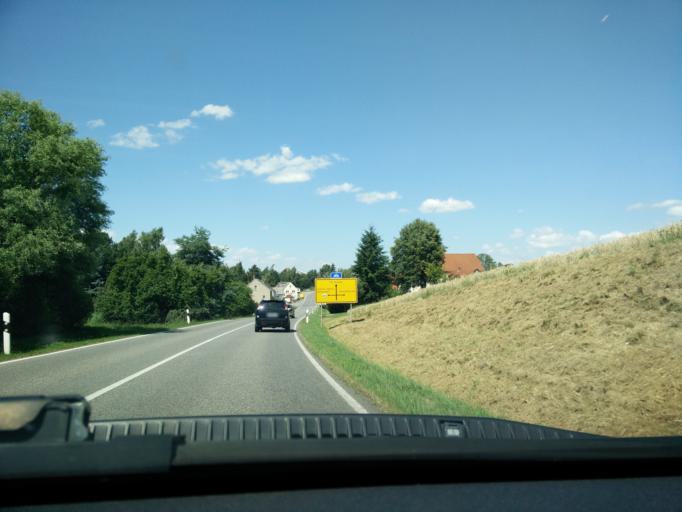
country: DE
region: Saxony
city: Narsdorf
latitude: 50.9877
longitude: 12.6993
